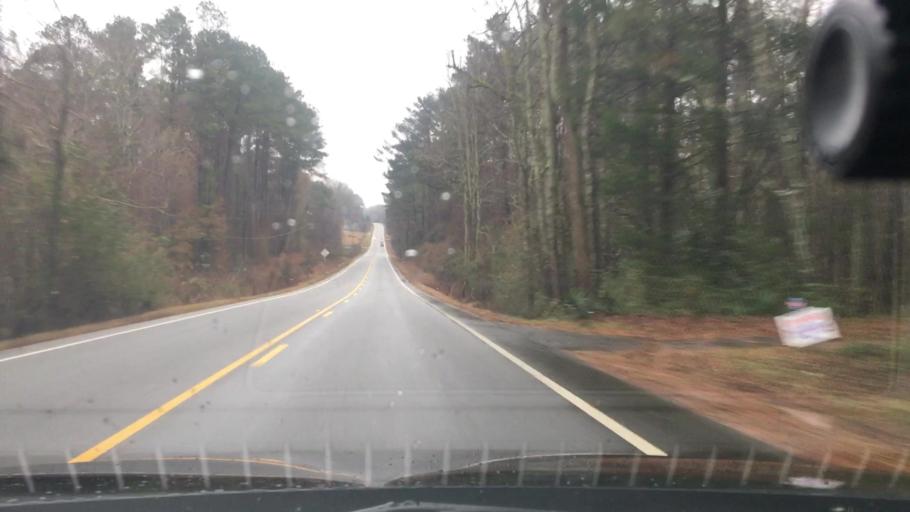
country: US
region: Georgia
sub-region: Spalding County
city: Experiment
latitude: 33.2409
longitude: -84.3408
